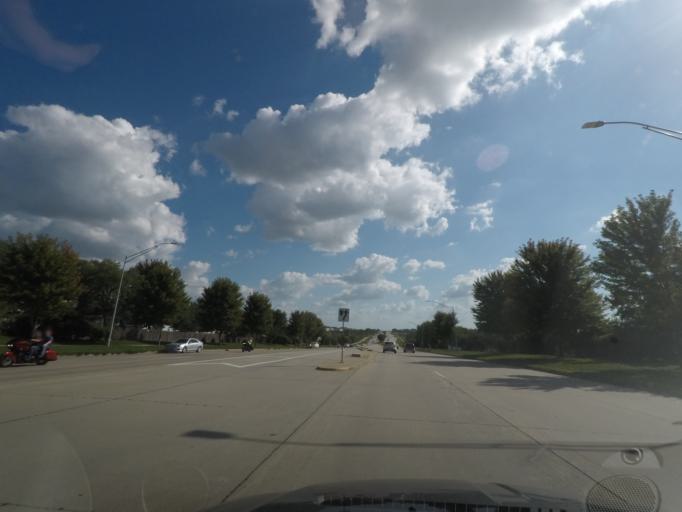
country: US
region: Iowa
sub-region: Dallas County
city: Waukee
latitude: 41.5785
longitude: -93.8093
